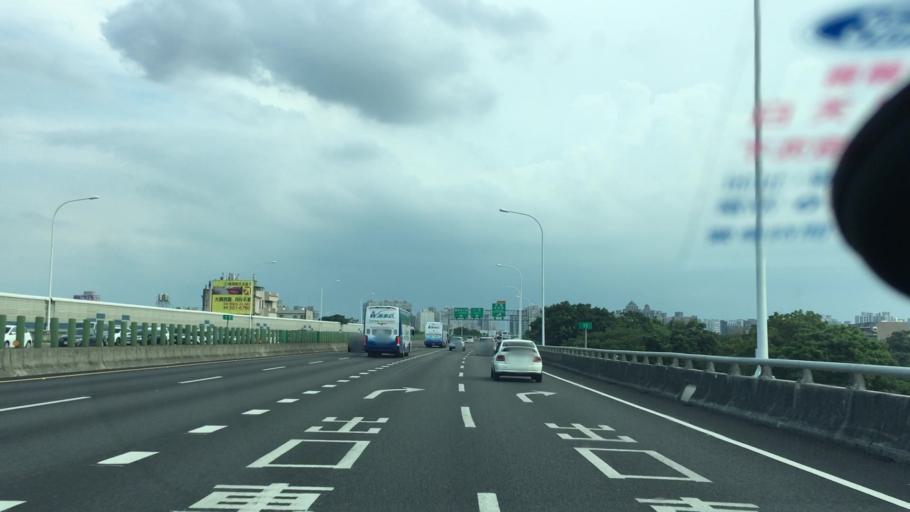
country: TW
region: Taiwan
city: Taoyuan City
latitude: 25.0046
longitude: 121.2827
